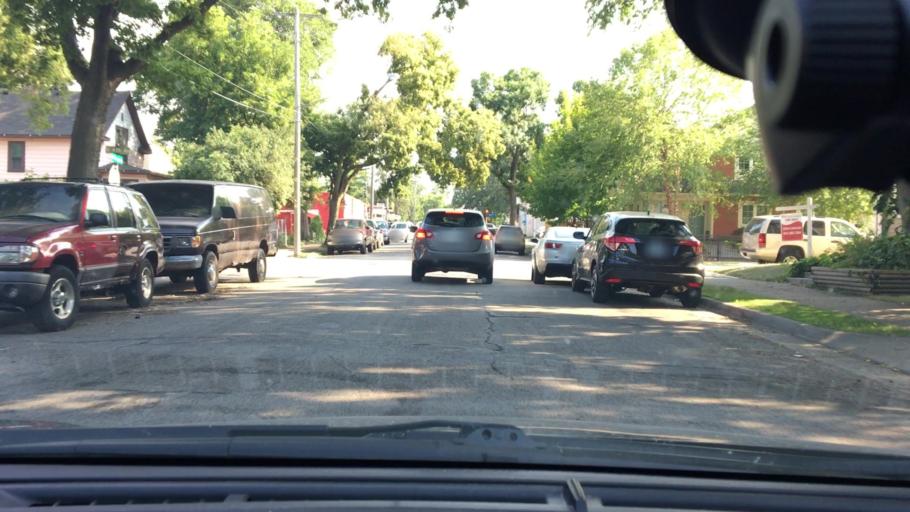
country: US
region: Minnesota
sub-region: Hennepin County
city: Minneapolis
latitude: 44.9819
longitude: -93.3046
